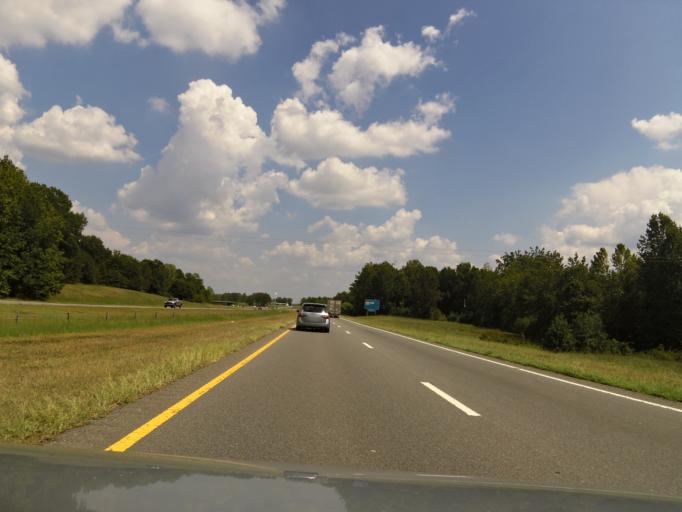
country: US
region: North Carolina
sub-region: Cleveland County
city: White Plains
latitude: 35.2461
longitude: -81.4163
